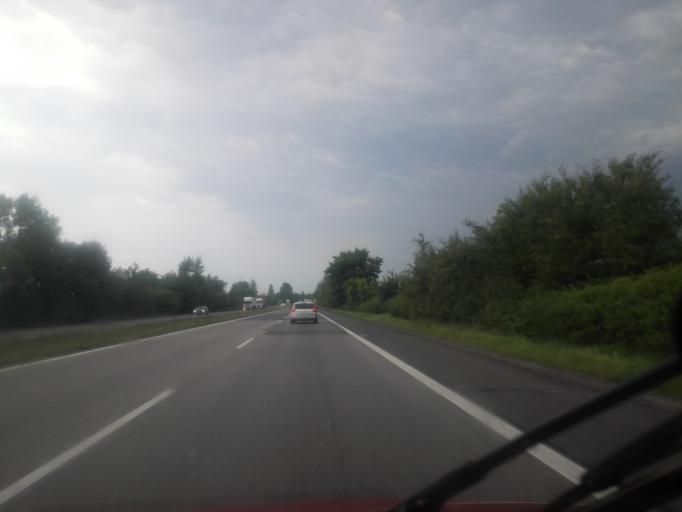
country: PL
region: Silesian Voivodeship
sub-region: Powiat czestochowski
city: Redziny
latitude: 50.8583
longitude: 19.1534
